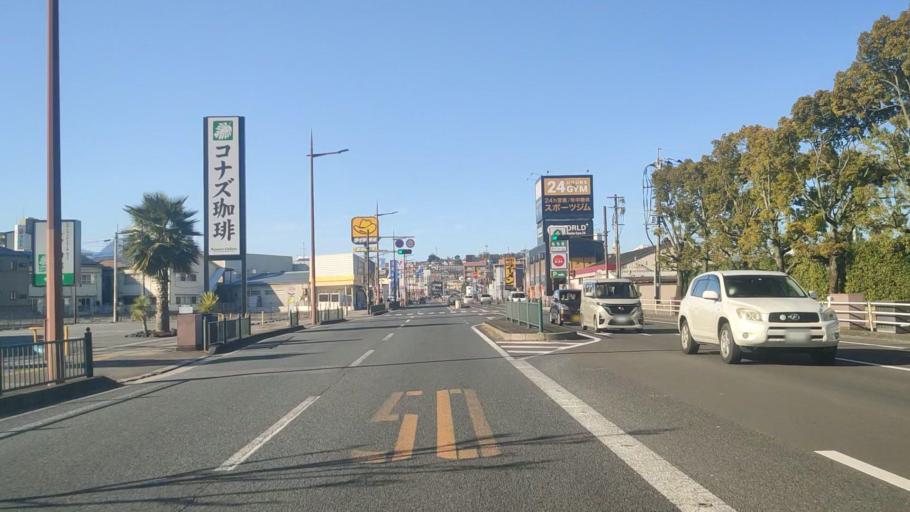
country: JP
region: Oita
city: Oita
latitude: 33.2085
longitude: 131.6002
